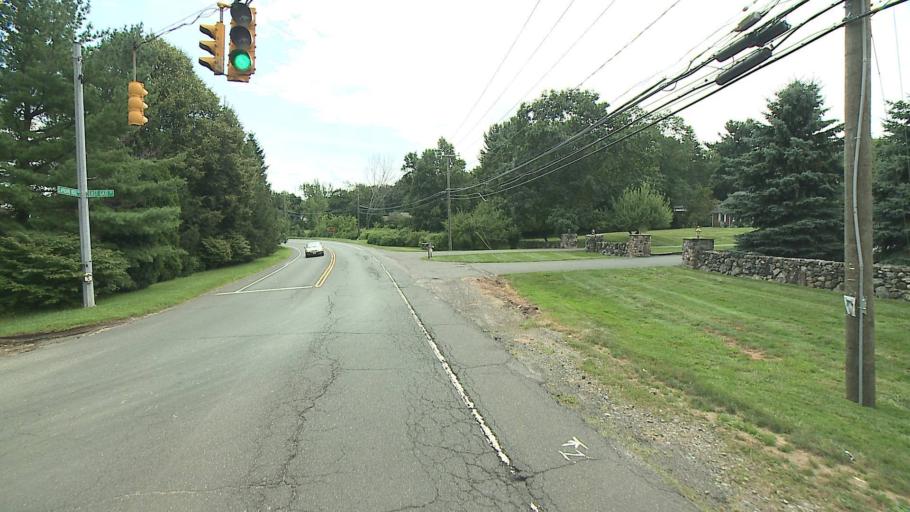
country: US
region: Connecticut
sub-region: Fairfield County
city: Danbury
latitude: 41.4181
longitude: -73.4749
